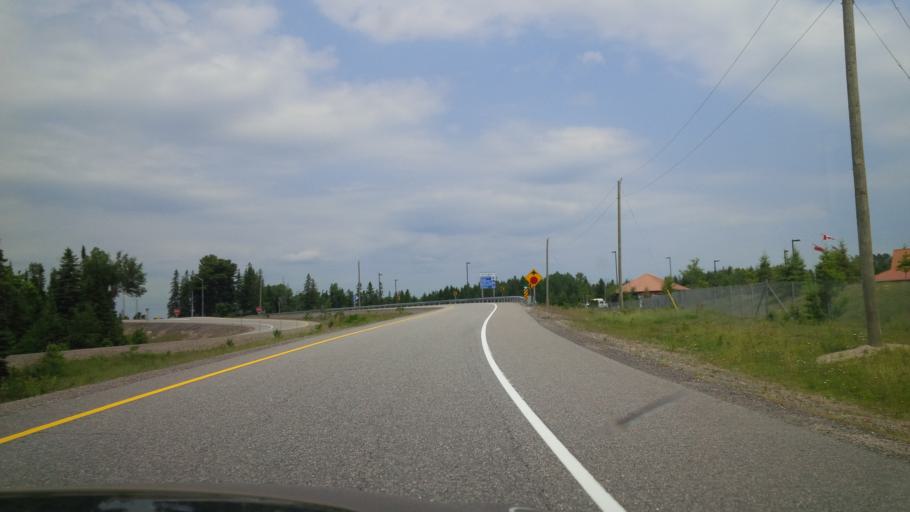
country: CA
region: Ontario
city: Huntsville
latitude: 45.5104
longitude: -79.3040
